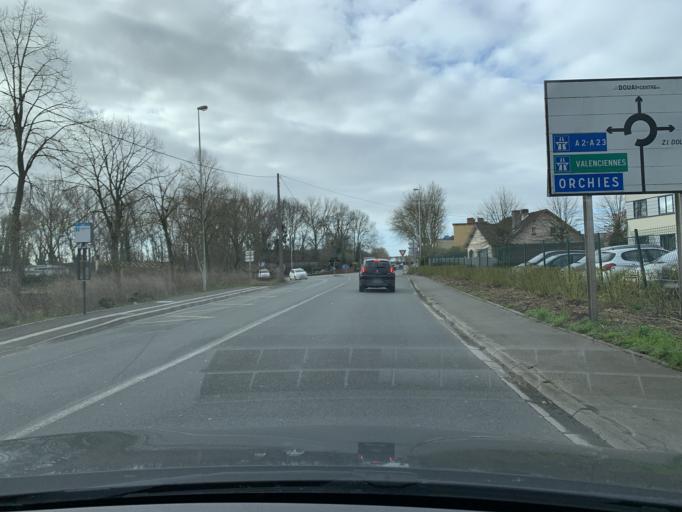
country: FR
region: Nord-Pas-de-Calais
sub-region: Departement du Nord
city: Waziers
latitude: 50.3981
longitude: 3.1039
